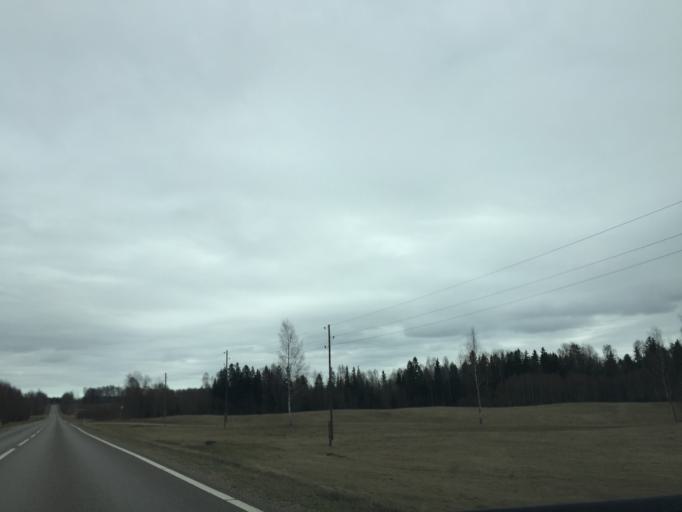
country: LV
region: Kraslavas Rajons
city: Kraslava
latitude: 55.9115
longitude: 27.0680
